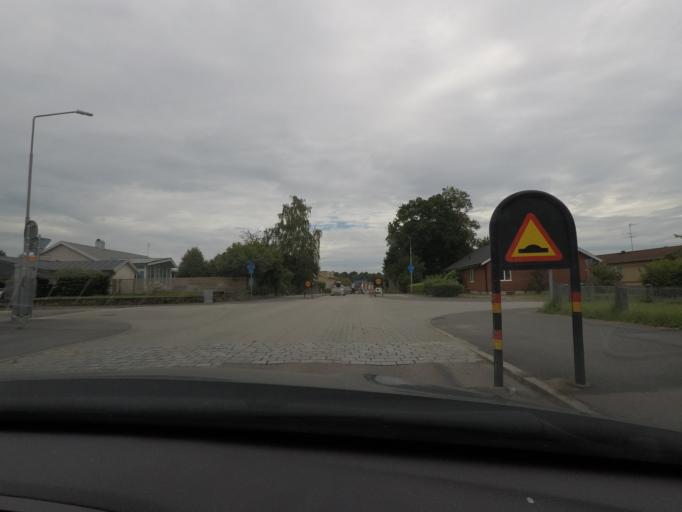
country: SE
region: Skane
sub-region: Osby Kommun
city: Osby
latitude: 56.3778
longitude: 14.0044
